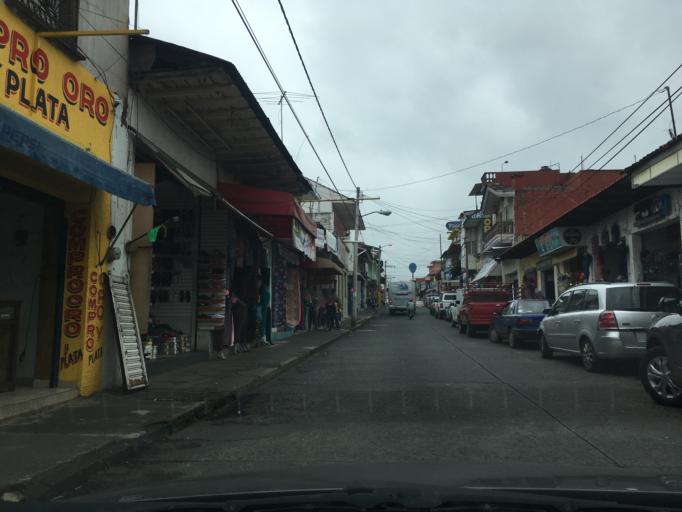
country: MX
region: Michoacan
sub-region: Uruapan
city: Uruapan
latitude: 19.4193
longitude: -102.0577
